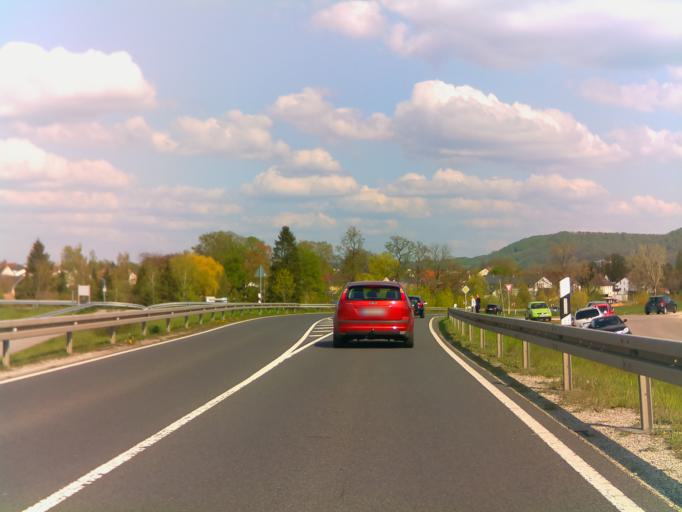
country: DE
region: Bavaria
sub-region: Upper Franconia
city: Coburg
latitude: 50.2768
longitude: 10.9413
